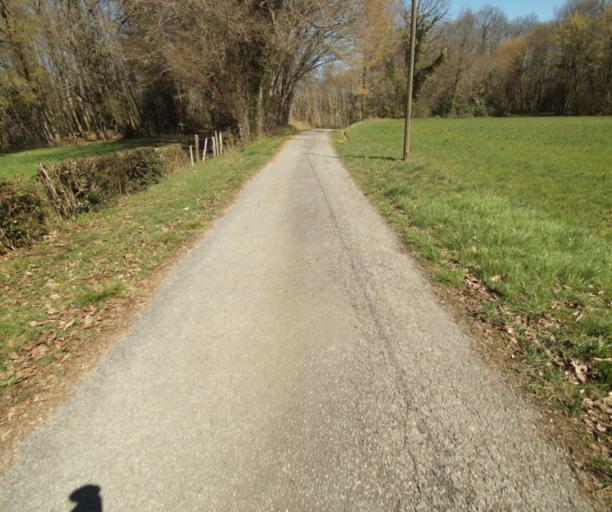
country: FR
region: Limousin
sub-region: Departement de la Correze
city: Chamboulive
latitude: 45.4011
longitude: 1.6668
